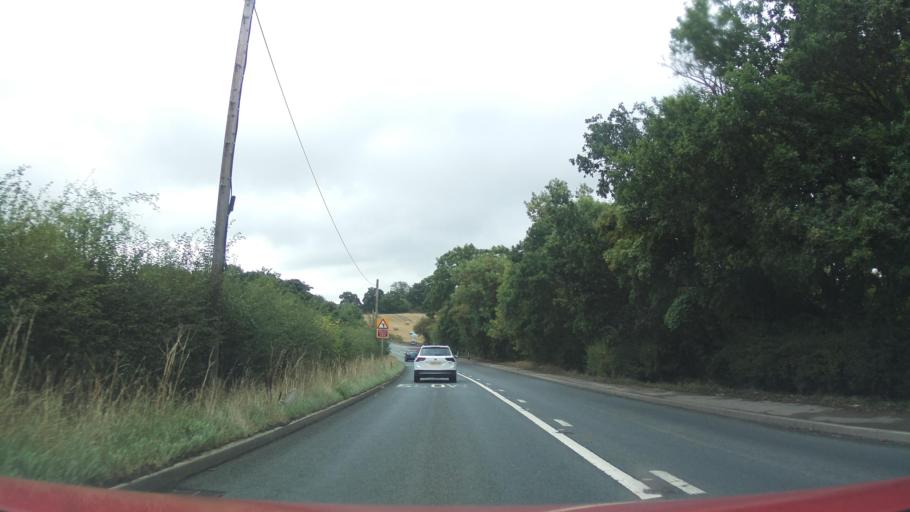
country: GB
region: England
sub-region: Kirklees
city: Clayton West
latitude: 53.6167
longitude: -1.5926
